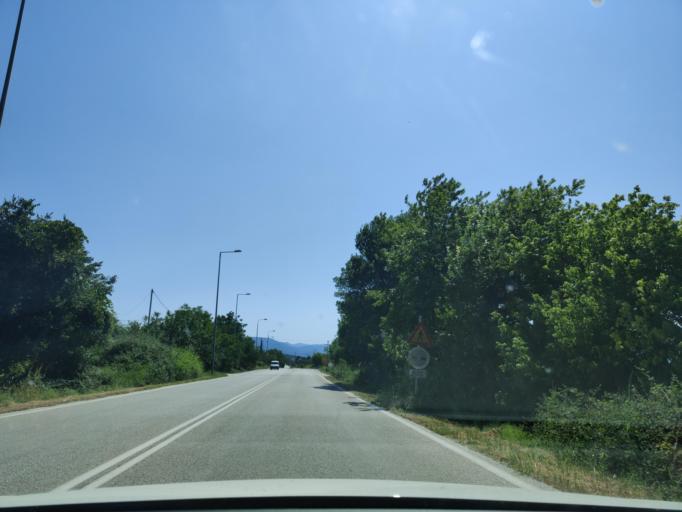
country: GR
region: East Macedonia and Thrace
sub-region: Nomos Kavalas
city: Zygos
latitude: 40.9886
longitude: 24.3754
